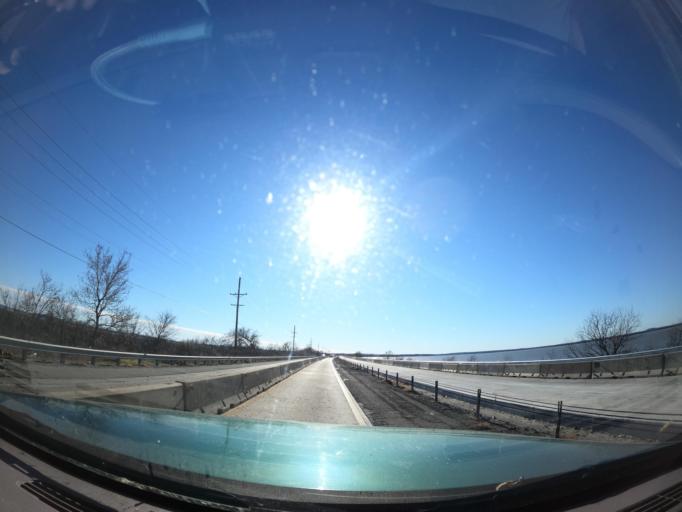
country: US
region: Oklahoma
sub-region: McIntosh County
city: Eufaula
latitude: 35.3483
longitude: -95.5801
